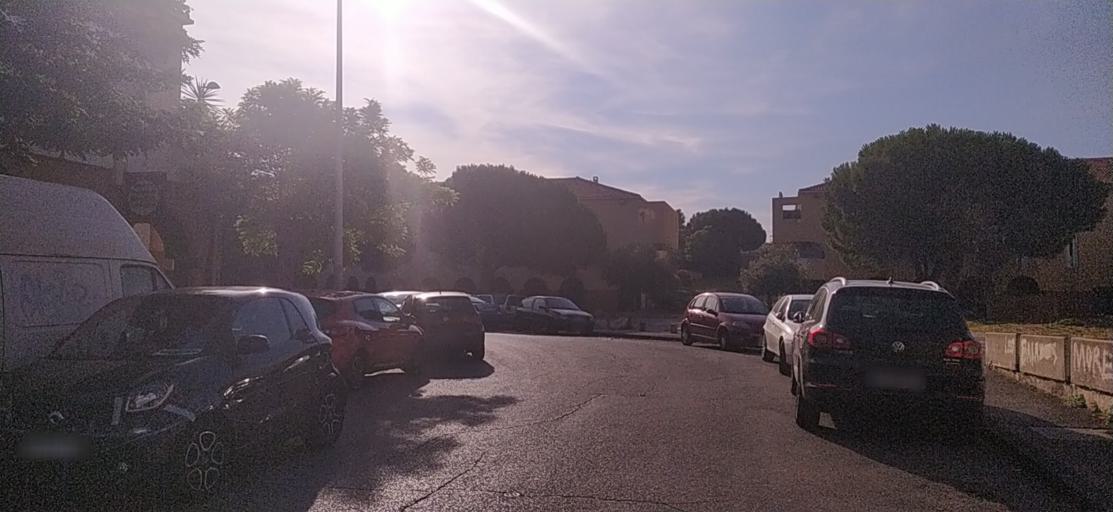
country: FR
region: Provence-Alpes-Cote d'Azur
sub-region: Departement des Bouches-du-Rhone
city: Marseille 16
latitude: 43.3525
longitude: 5.3410
